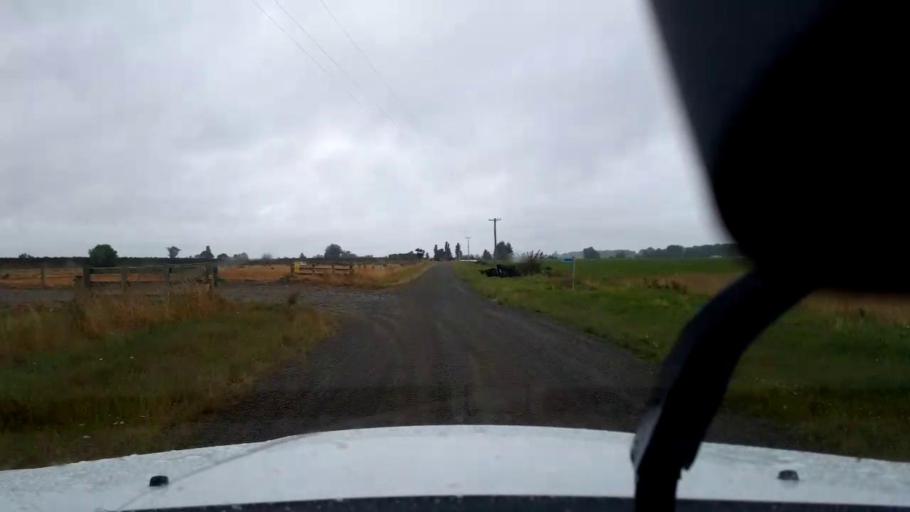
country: NZ
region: Canterbury
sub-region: Timaru District
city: Pleasant Point
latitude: -44.2533
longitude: 171.2080
